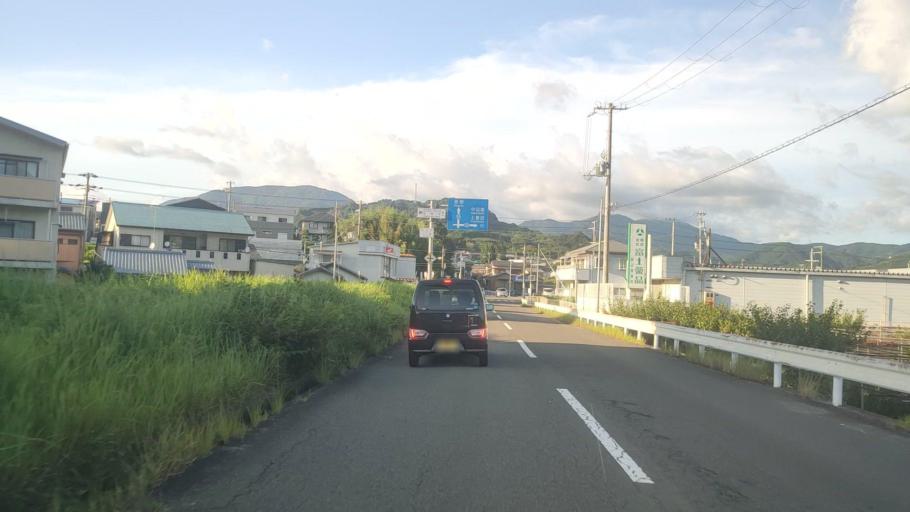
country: JP
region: Wakayama
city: Tanabe
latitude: 33.7341
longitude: 135.4184
